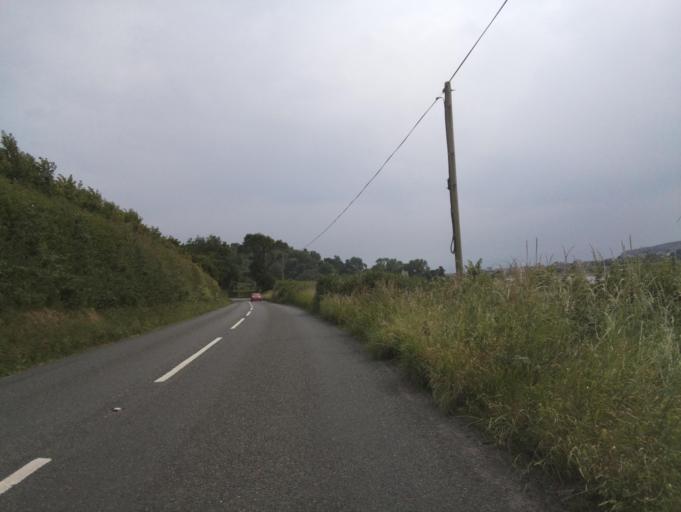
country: GB
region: England
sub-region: Devon
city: Colyton
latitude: 50.7186
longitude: -3.0523
